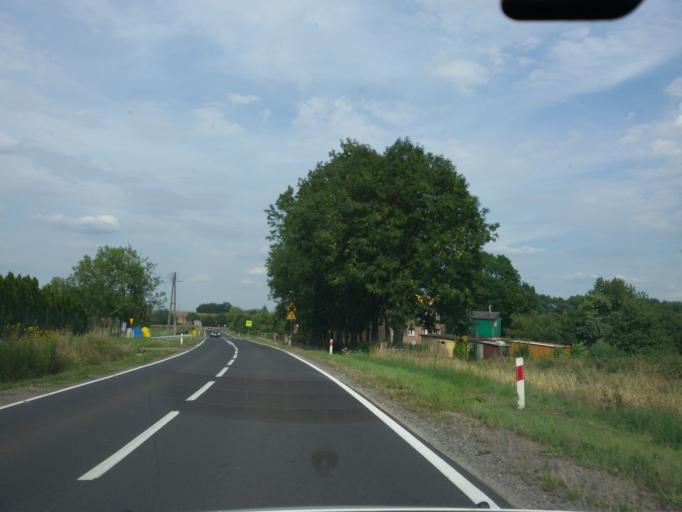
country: PL
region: Lower Silesian Voivodeship
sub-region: Powiat polkowicki
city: Radwanice
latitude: 51.6289
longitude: 15.9617
